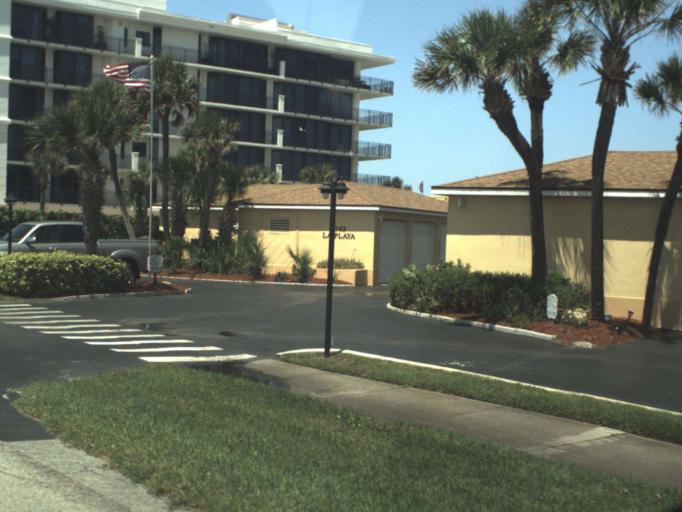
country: US
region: Florida
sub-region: Brevard County
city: Satellite Beach
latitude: 28.1745
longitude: -80.5900
